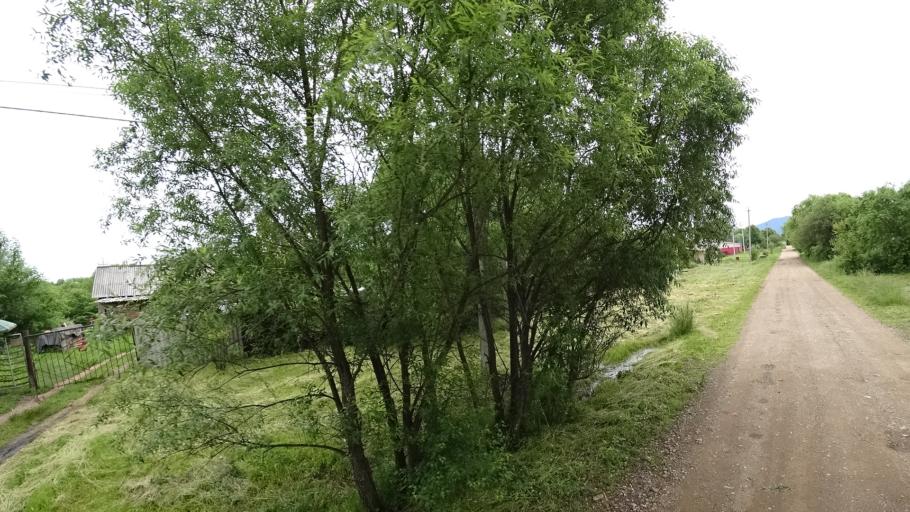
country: RU
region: Primorskiy
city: Arsen'yev
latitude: 44.1891
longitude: 133.3073
